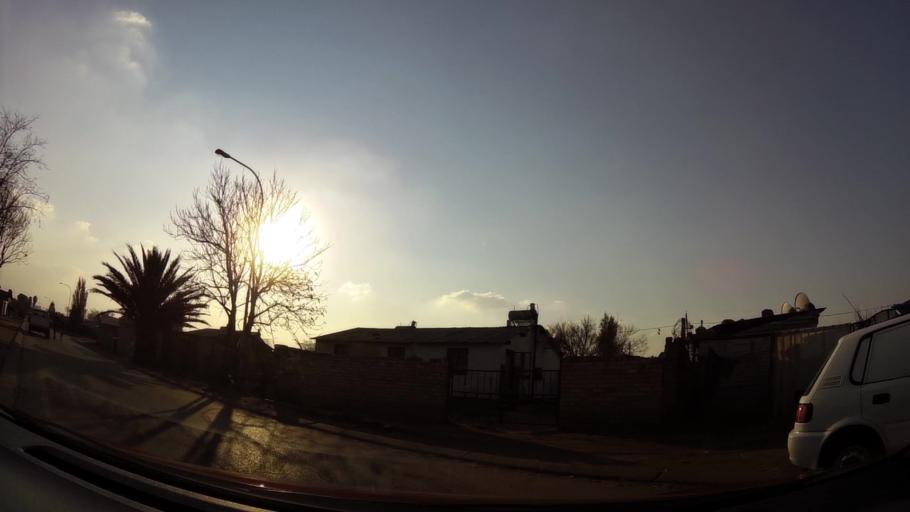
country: ZA
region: Gauteng
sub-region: City of Johannesburg Metropolitan Municipality
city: Soweto
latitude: -26.2900
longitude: 27.8949
